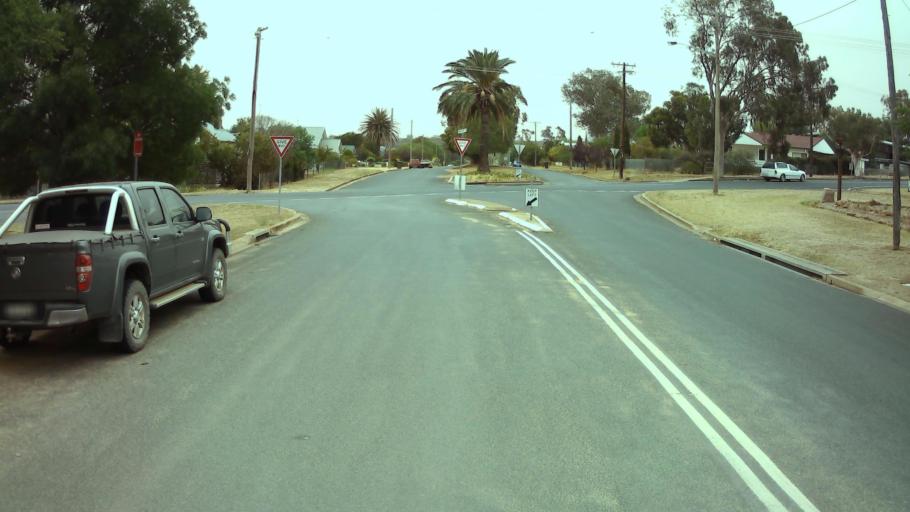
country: AU
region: New South Wales
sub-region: Weddin
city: Grenfell
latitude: -33.8959
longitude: 148.1656
